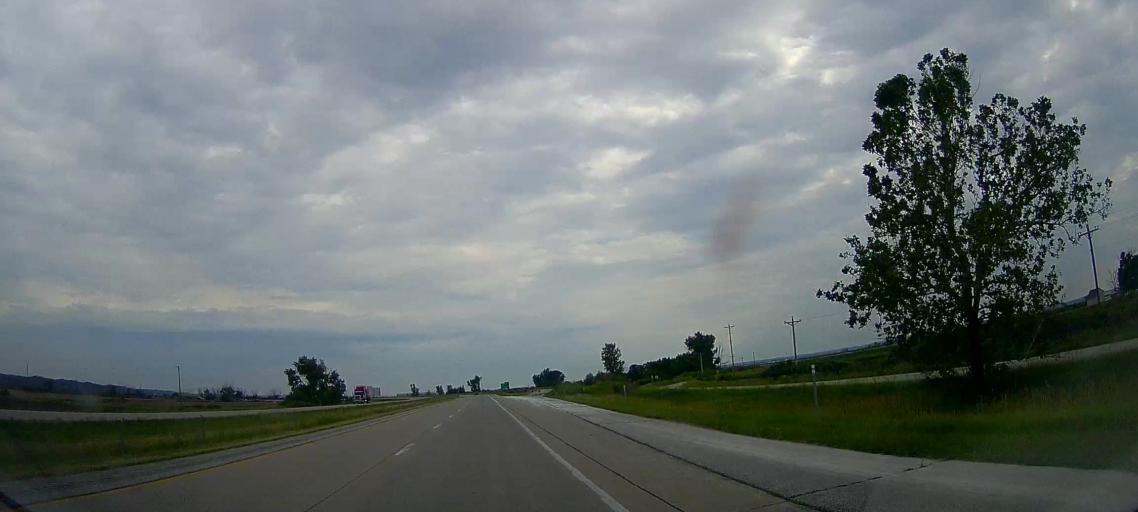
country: US
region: Iowa
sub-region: Harrison County
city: Missouri Valley
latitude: 41.5221
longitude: -95.9179
